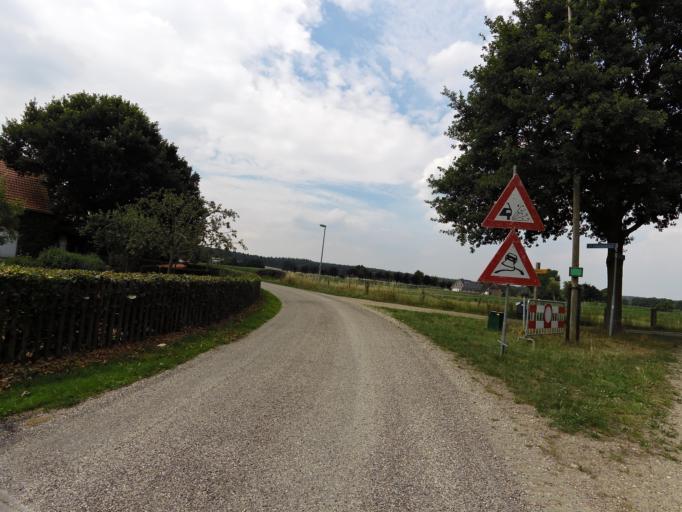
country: NL
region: Gelderland
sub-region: Gemeente Montferland
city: s-Heerenberg
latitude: 51.8806
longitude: 6.2211
